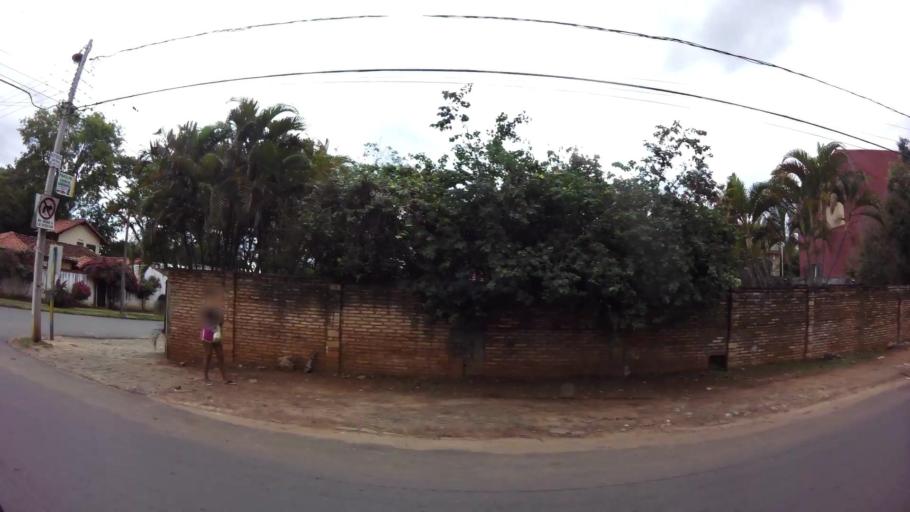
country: PY
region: Central
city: San Lorenzo
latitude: -25.2742
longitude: -57.4944
